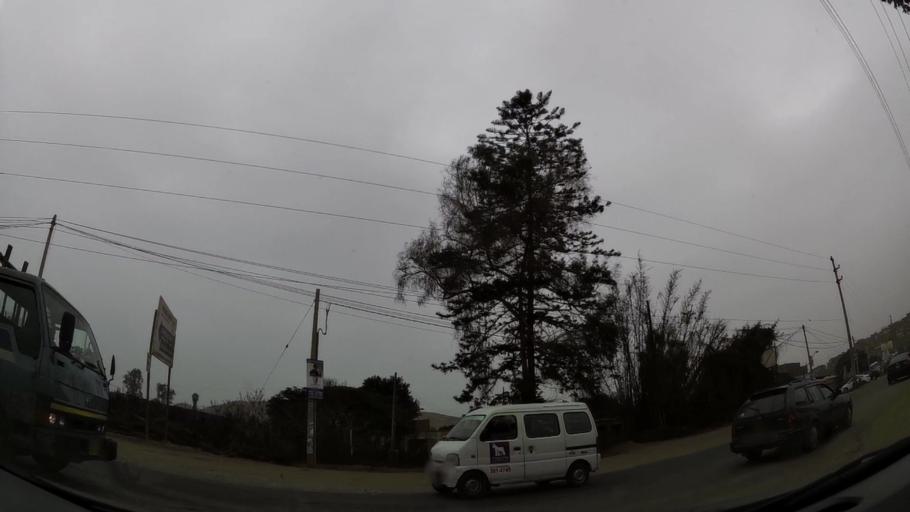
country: PE
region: Lima
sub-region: Lima
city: Punta Hermosa
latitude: -12.2543
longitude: -76.8912
